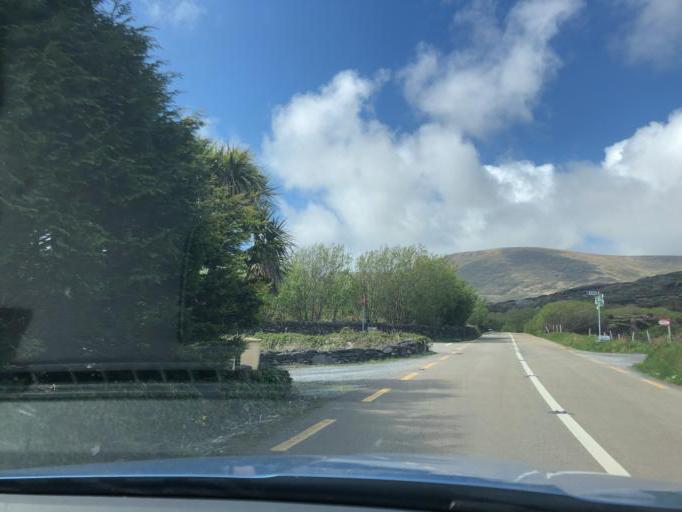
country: IE
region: Munster
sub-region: Ciarrai
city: Cahersiveen
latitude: 51.7606
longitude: -10.0956
